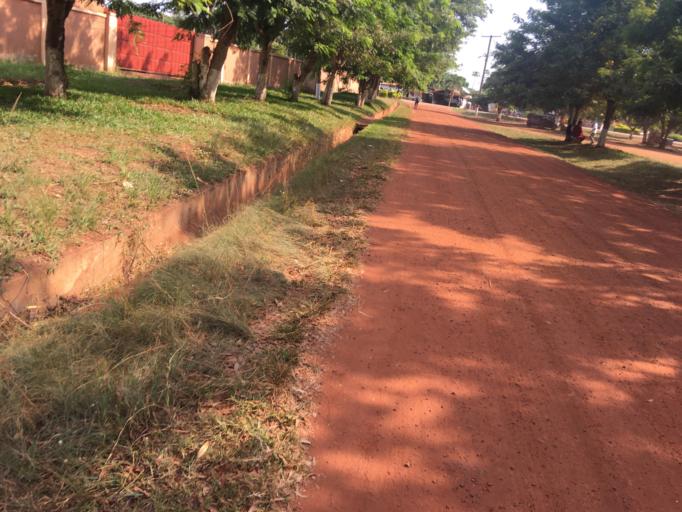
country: GH
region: Brong-Ahafo
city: Techiman
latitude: 7.5843
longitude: -1.9266
